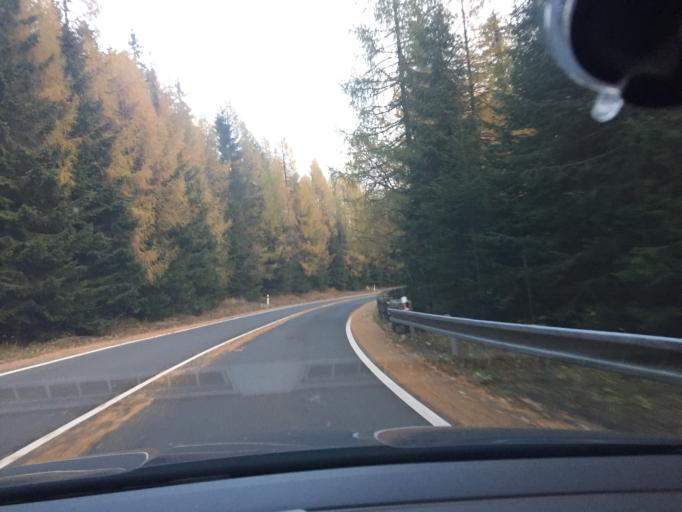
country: SK
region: Presovsky
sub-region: Okres Poprad
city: Strba
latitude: 49.1121
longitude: 20.0730
